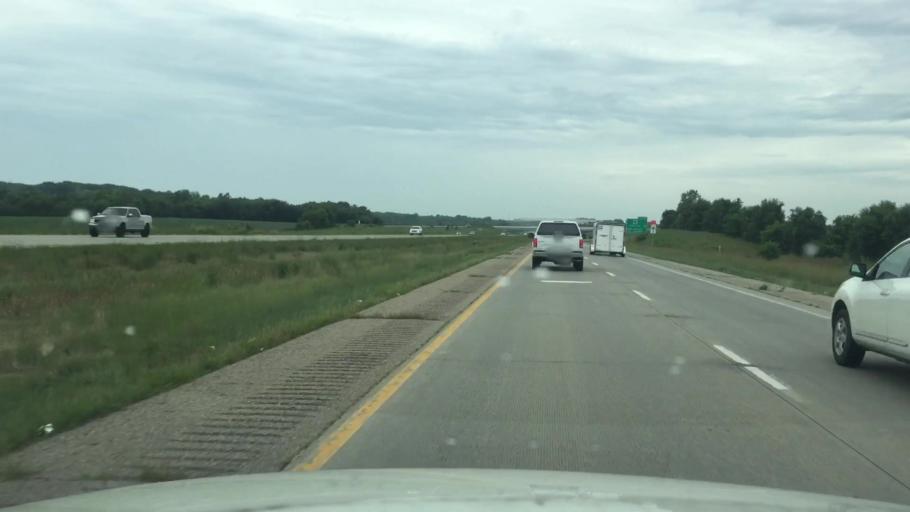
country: US
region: Iowa
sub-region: Warren County
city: Norwalk
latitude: 41.5030
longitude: -93.6350
